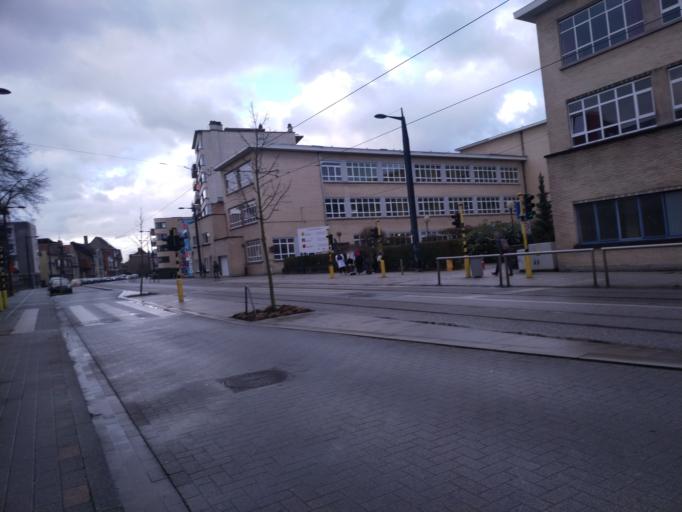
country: BE
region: Flanders
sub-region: Provincie Oost-Vlaanderen
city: Gent
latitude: 51.0335
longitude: 3.7079
